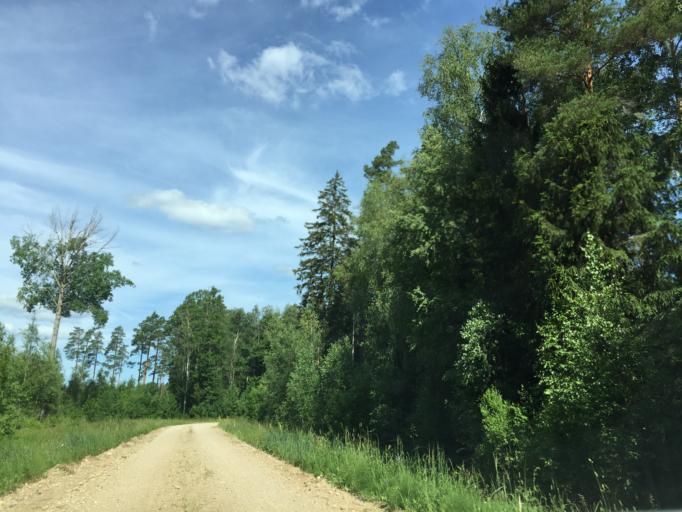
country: LV
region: Dundaga
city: Dundaga
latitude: 57.4255
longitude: 22.0751
